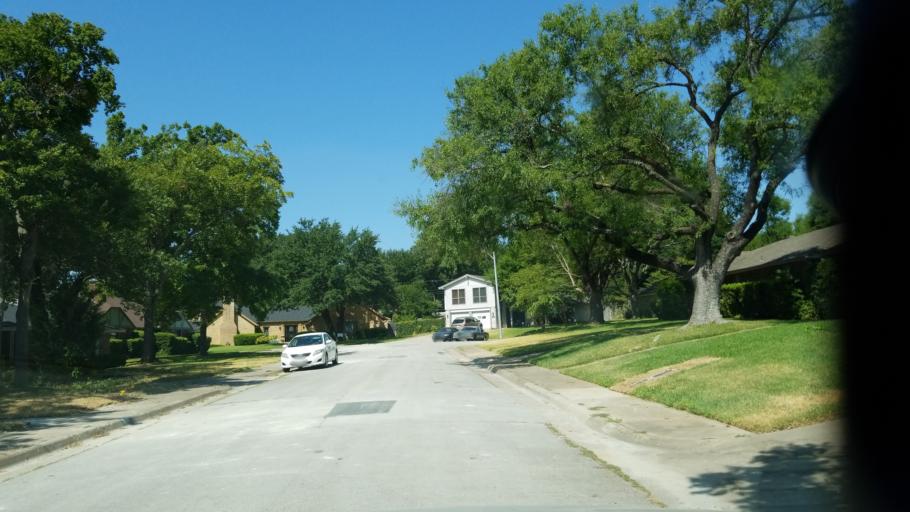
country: US
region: Texas
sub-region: Dallas County
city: Duncanville
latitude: 32.6461
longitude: -96.8973
